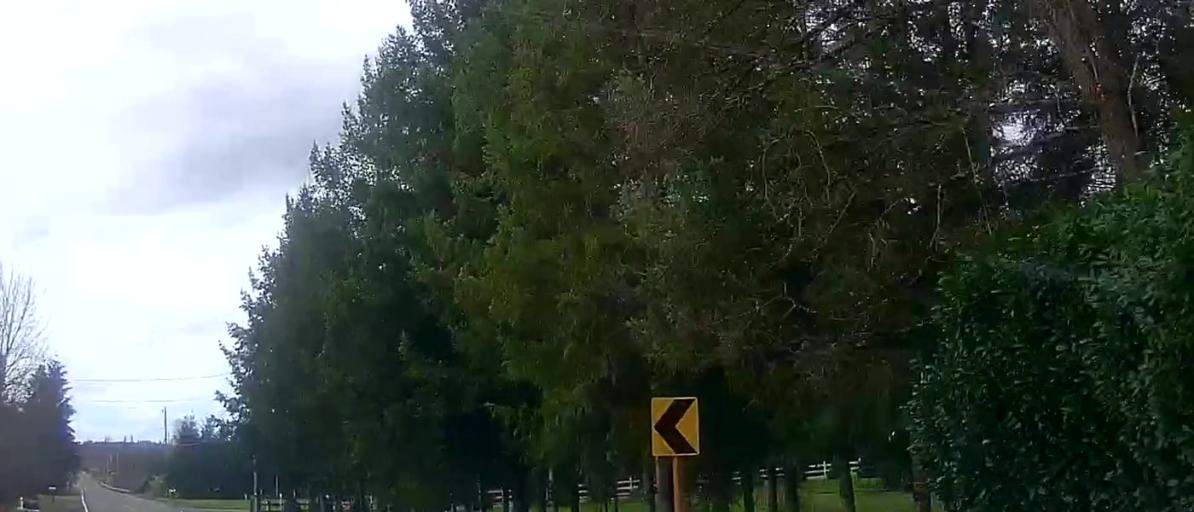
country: US
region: Washington
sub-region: Skagit County
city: Sedro-Woolley
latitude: 48.5834
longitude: -122.2574
